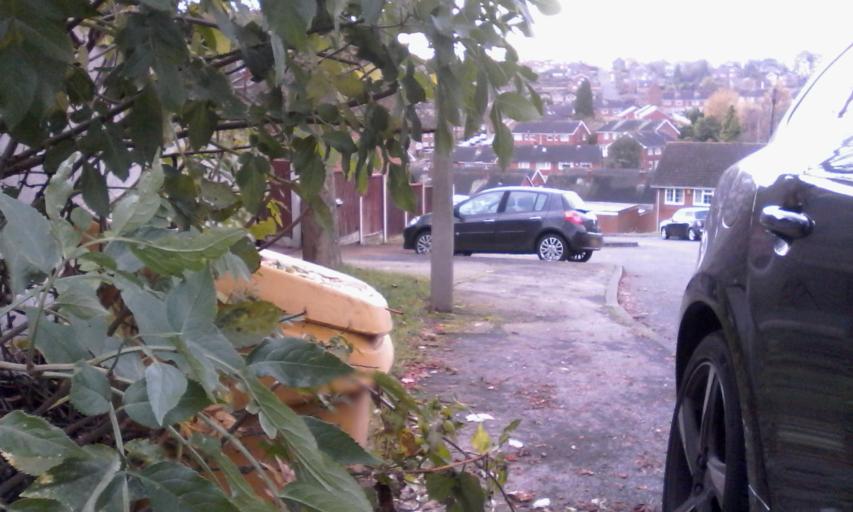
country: GB
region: England
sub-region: Nottinghamshire
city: Arnold
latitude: 52.9851
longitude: -1.0945
